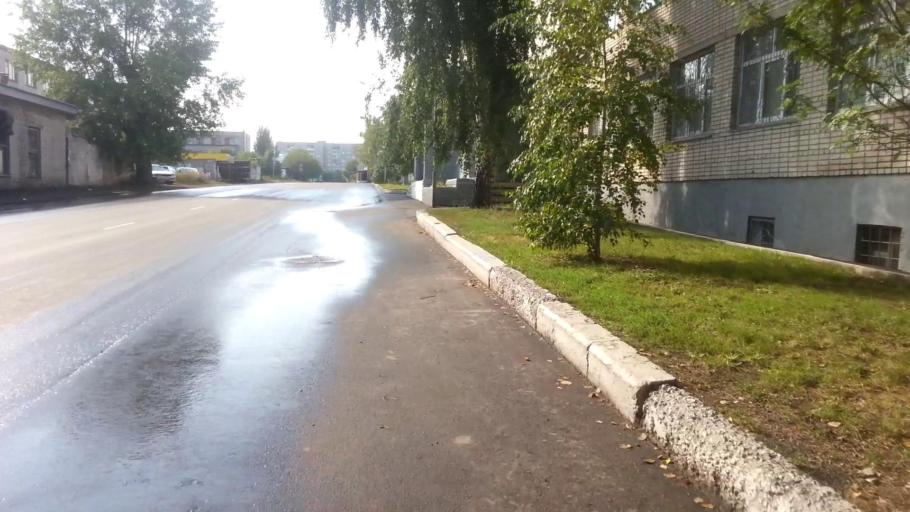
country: RU
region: Altai Krai
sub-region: Gorod Barnaulskiy
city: Barnaul
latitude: 53.3448
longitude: 83.7173
